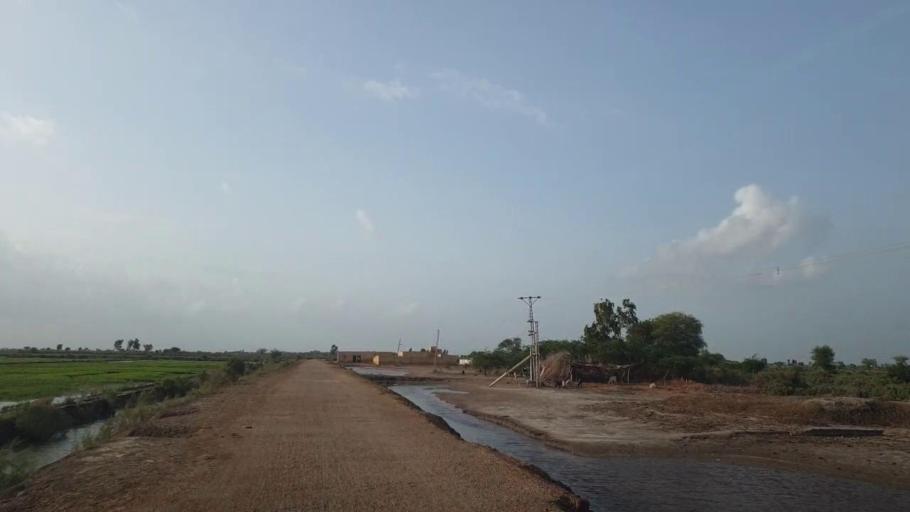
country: PK
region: Sindh
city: Tando Bago
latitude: 24.6601
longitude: 69.1119
